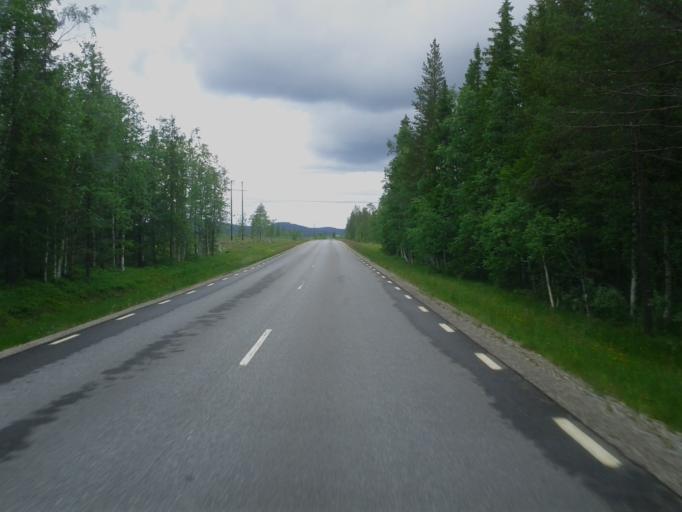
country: SE
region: Vaesterbotten
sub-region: Mala Kommun
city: Mala
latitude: 65.0677
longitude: 19.0347
